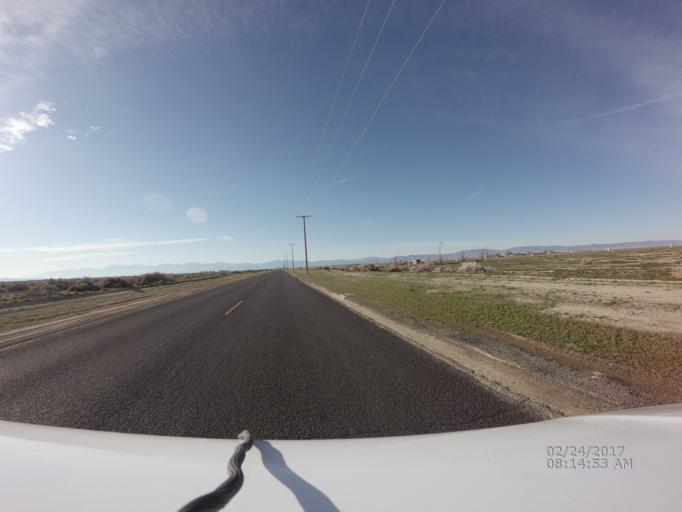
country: US
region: California
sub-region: Los Angeles County
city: Lancaster
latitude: 34.7385
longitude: -118.0412
